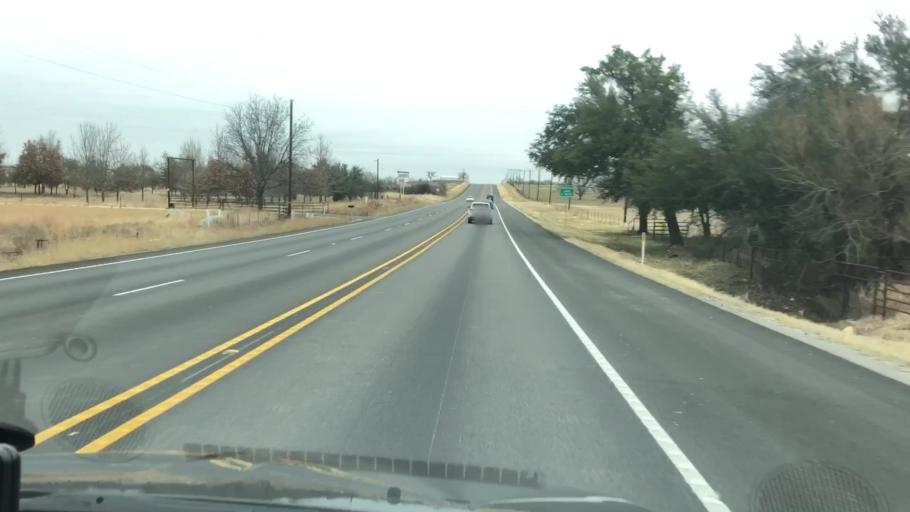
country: US
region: Texas
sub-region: Erath County
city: Stephenville
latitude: 32.2894
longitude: -98.1911
